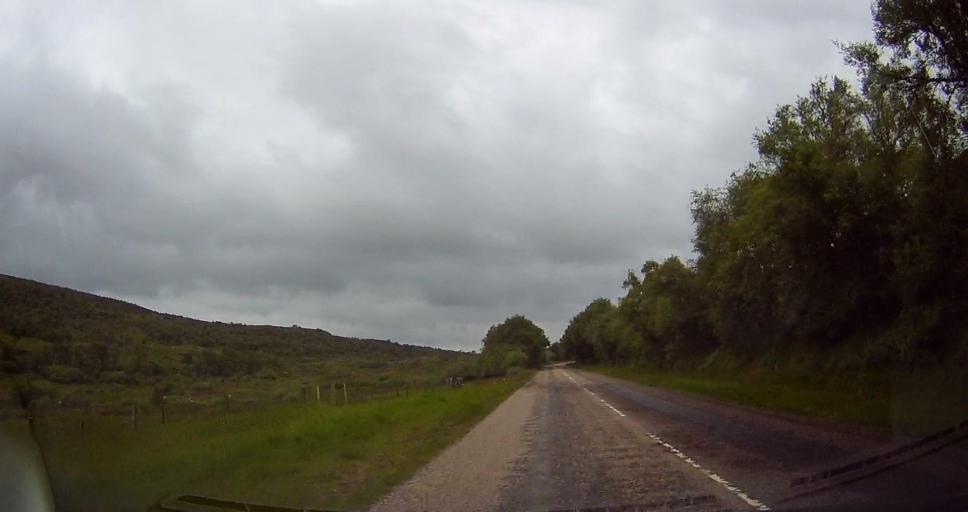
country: GB
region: Scotland
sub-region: Highland
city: Dornoch
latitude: 58.0170
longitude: -4.3212
